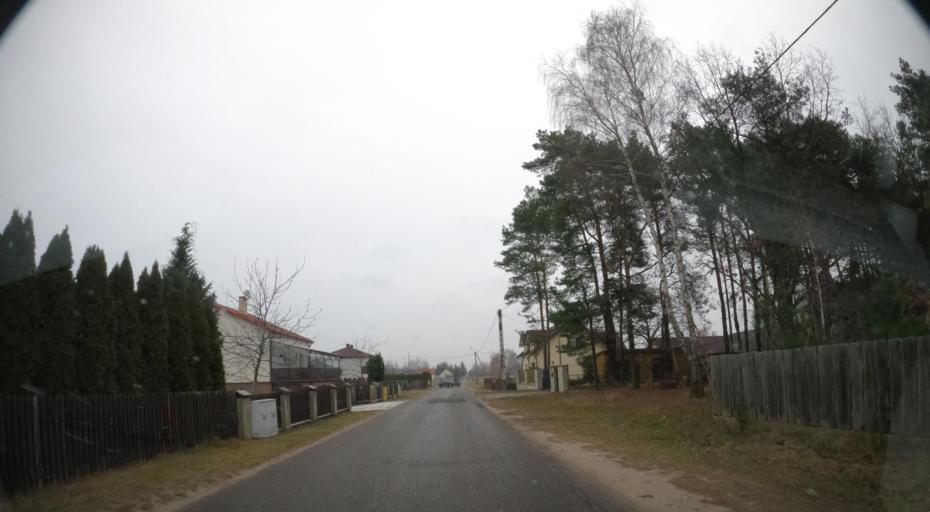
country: PL
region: Masovian Voivodeship
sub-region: Powiat radomski
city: Jedlnia-Letnisko
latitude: 51.4153
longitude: 21.2616
